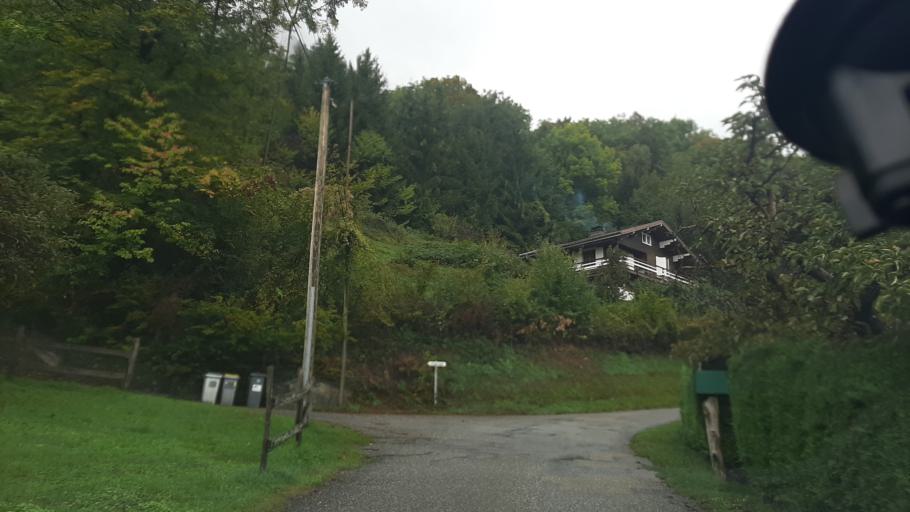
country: FR
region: Rhone-Alpes
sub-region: Departement de la Savoie
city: Gresy-sur-Isere
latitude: 45.6187
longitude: 6.2765
